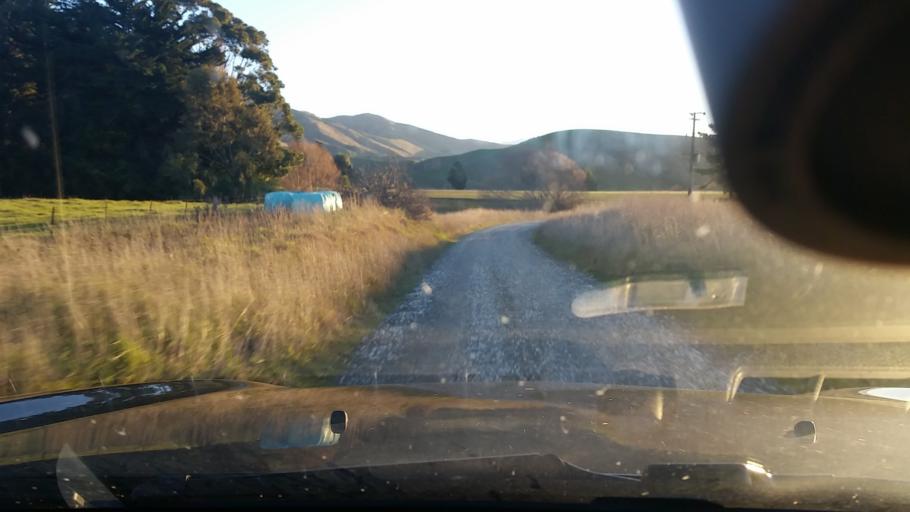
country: NZ
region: Marlborough
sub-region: Marlborough District
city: Blenheim
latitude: -41.7385
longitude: 174.0449
